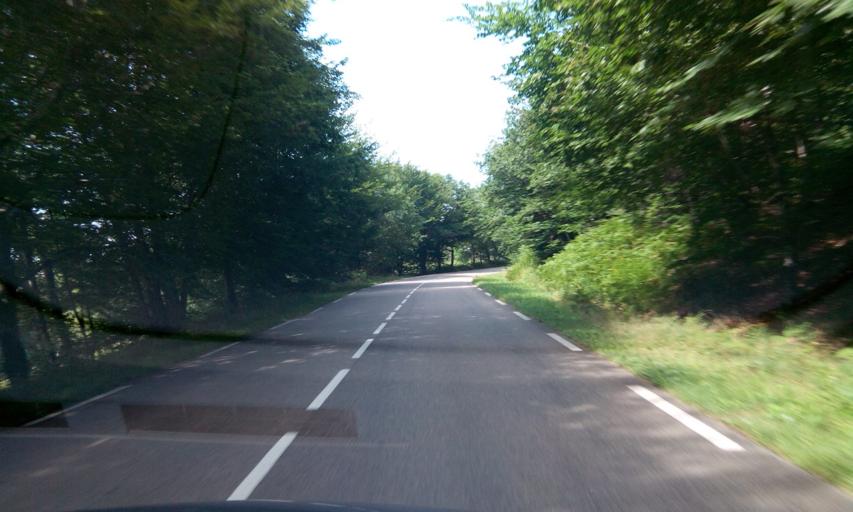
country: FR
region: Limousin
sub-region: Departement de la Correze
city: Beynat
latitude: 45.1193
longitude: 1.7853
